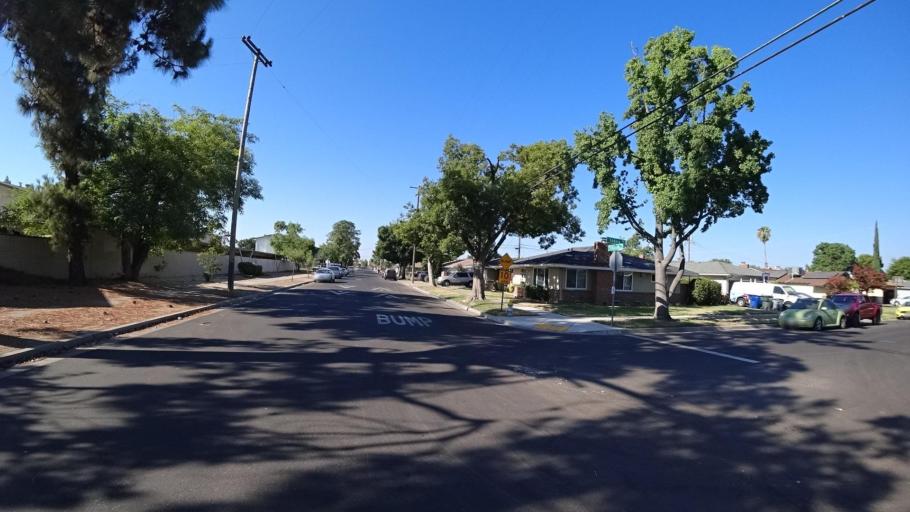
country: US
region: California
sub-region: Fresno County
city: Fresno
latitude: 36.7839
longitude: -119.7556
